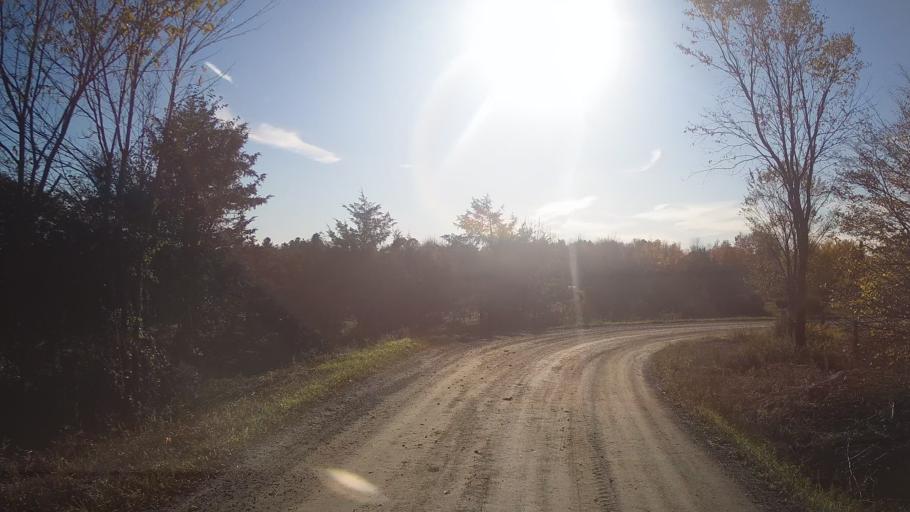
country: CA
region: Ontario
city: Perth
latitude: 44.7059
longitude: -76.4285
